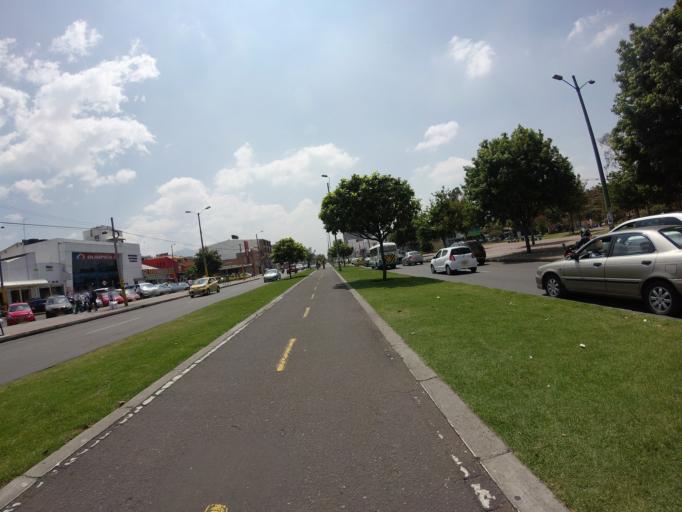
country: CO
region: Bogota D.C.
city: Barrio San Luis
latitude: 4.7212
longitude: -74.0466
